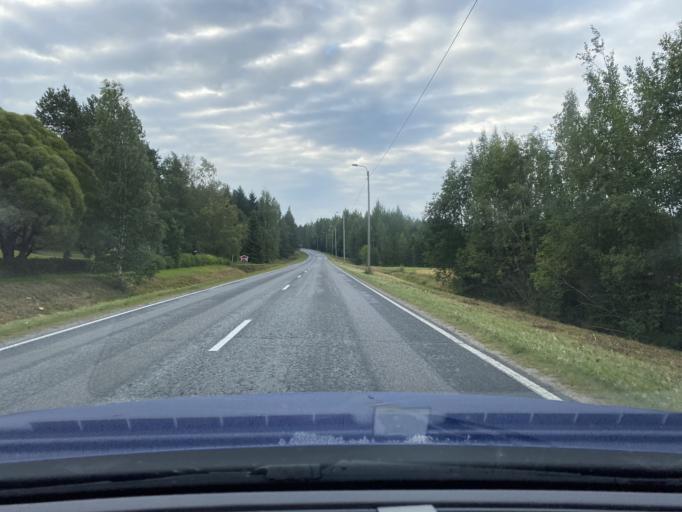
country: FI
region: Southern Ostrobothnia
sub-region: Seinaejoki
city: Jurva
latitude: 62.6804
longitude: 21.9751
